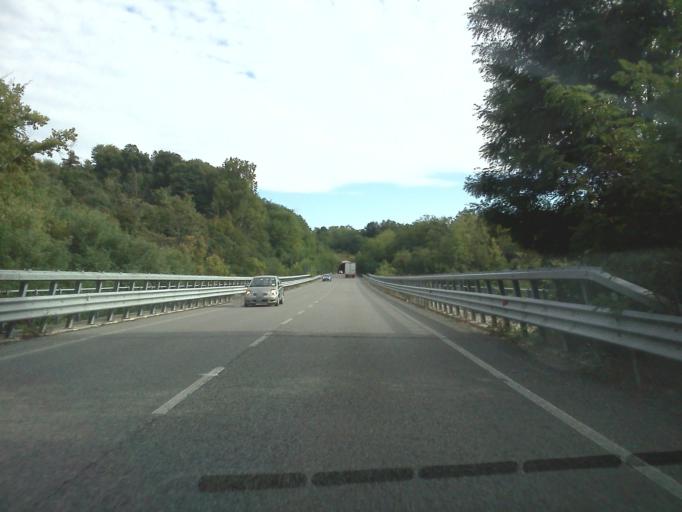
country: IT
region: Piedmont
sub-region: Provincia di Biella
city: Vallanzengo
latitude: 45.6101
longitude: 8.1597
